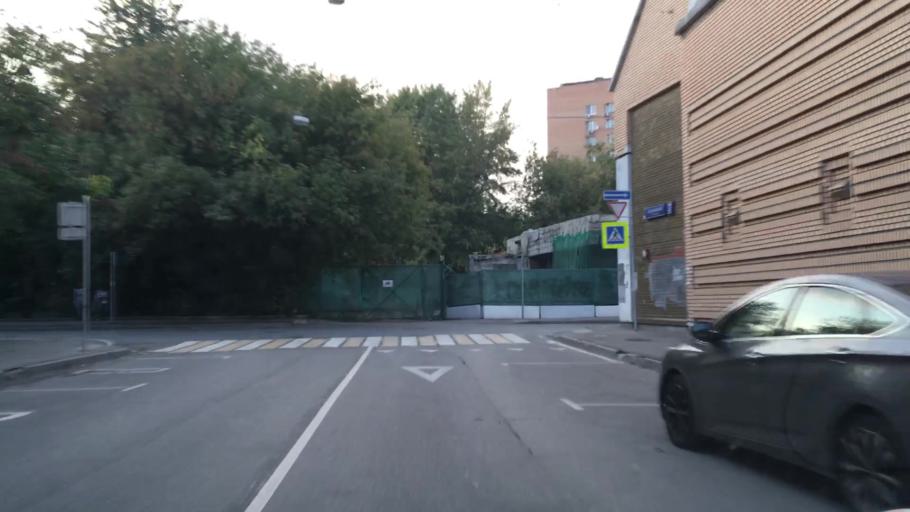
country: RU
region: Moscow
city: Moscow
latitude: 55.7279
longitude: 37.6038
